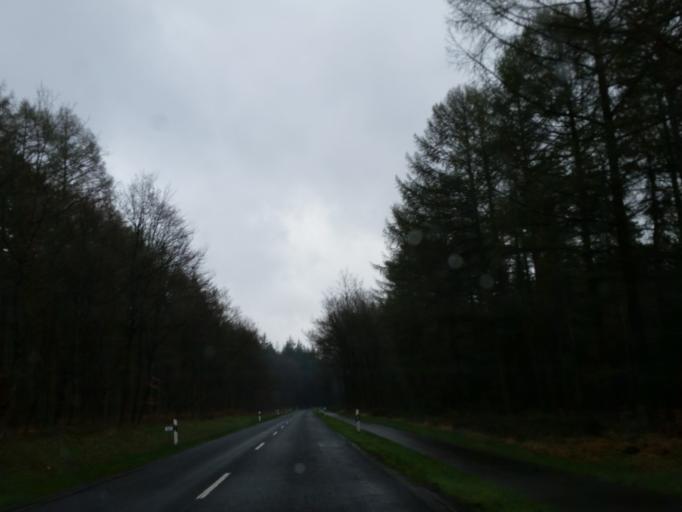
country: DE
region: Lower Saxony
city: Hipstedt
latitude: 53.5016
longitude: 8.9895
